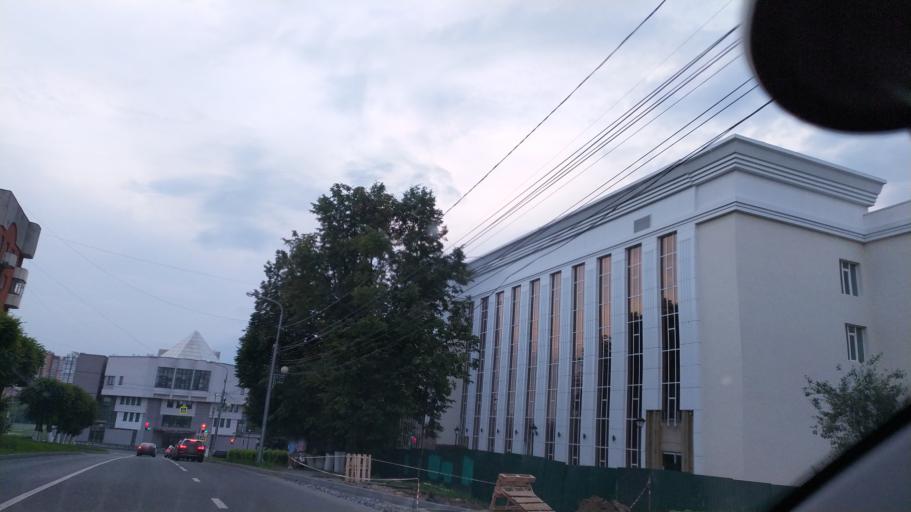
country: RU
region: Chuvashia
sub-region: Cheboksarskiy Rayon
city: Cheboksary
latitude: 56.1421
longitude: 47.2472
